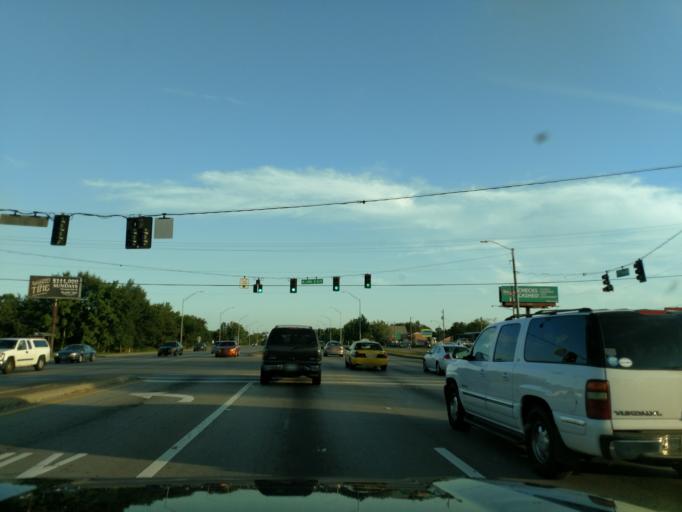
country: US
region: Mississippi
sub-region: Harrison County
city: West Gulfport
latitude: 30.4044
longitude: -89.0929
